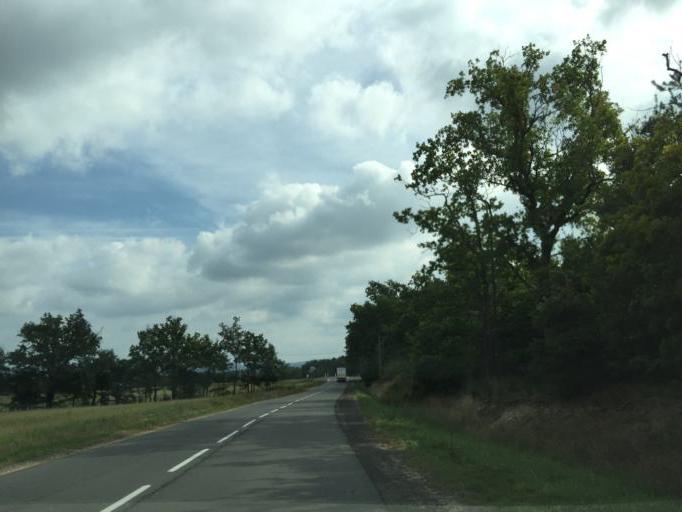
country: FR
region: Rhone-Alpes
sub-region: Departement de la Loire
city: Saint-Romain-le-Puy
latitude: 45.5374
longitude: 4.1490
